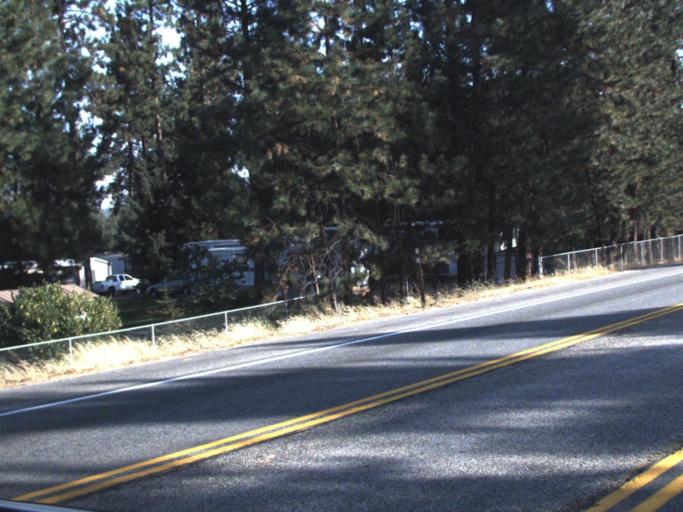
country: US
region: Washington
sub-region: Spokane County
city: Deer Park
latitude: 47.9735
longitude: -117.3496
